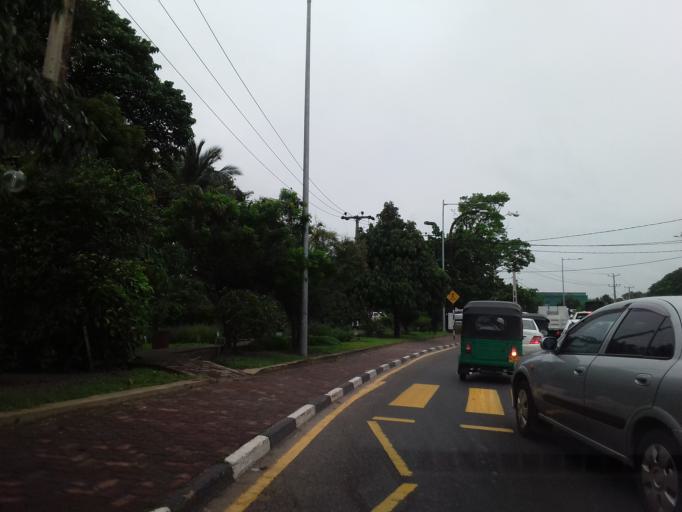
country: LK
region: Western
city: Battaramulla South
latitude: 6.8931
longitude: 79.9213
